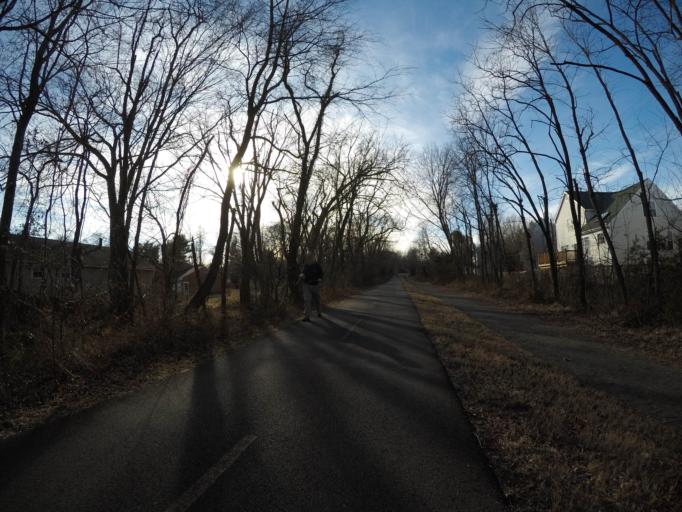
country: US
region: Virginia
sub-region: Loudoun County
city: Leesburg
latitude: 39.1110
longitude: -77.5847
